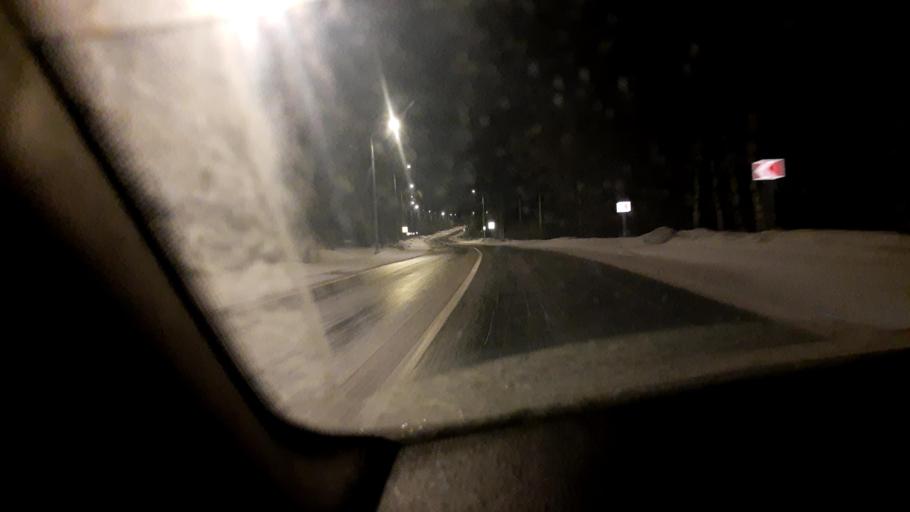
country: RU
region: Moskovskaya
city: Shemetovo
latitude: 56.5149
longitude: 38.1171
